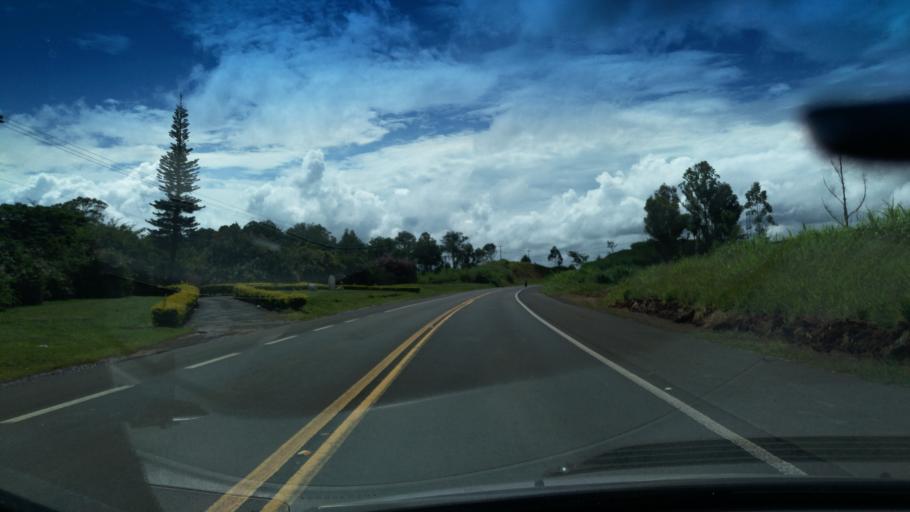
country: BR
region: Sao Paulo
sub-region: Santo Antonio Do Jardim
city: Espirito Santo do Pinhal
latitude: -22.1420
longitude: -46.7125
